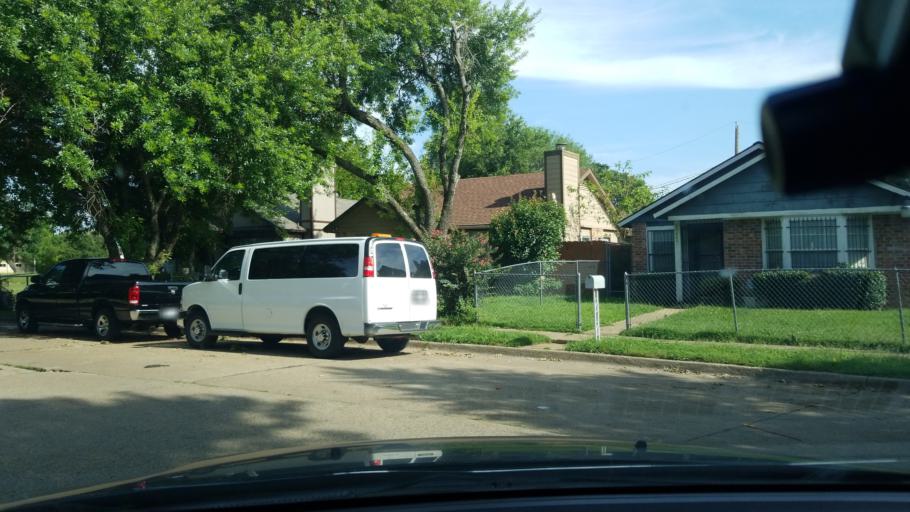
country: US
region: Texas
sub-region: Dallas County
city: Balch Springs
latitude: 32.7161
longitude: -96.6406
